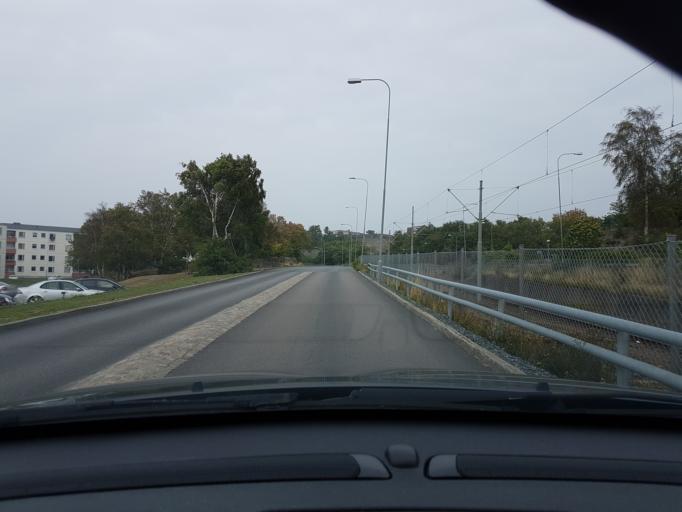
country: SE
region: Vaestra Goetaland
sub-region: Goteborg
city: Majorna
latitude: 57.6460
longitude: 11.9002
